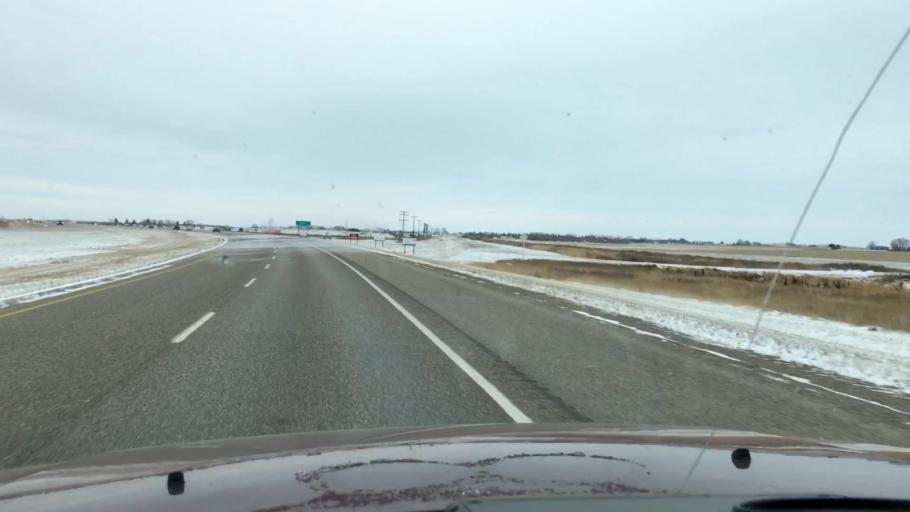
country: CA
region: Saskatchewan
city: Watrous
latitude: 51.0674
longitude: -105.8367
